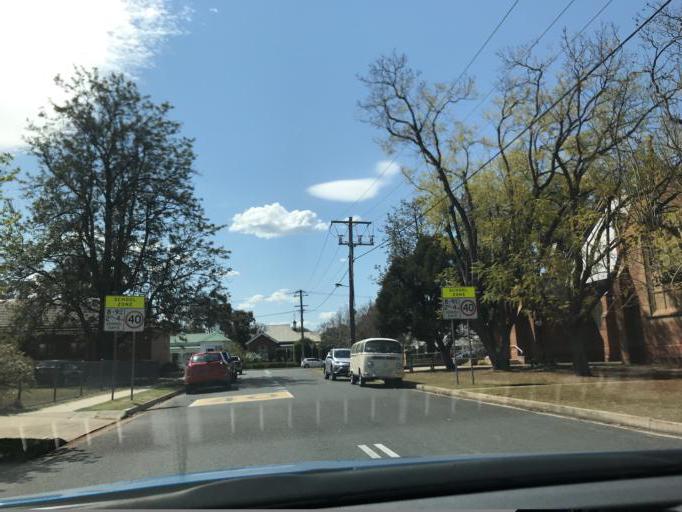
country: AU
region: New South Wales
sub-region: Singleton
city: Singleton
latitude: -32.5645
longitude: 151.1728
